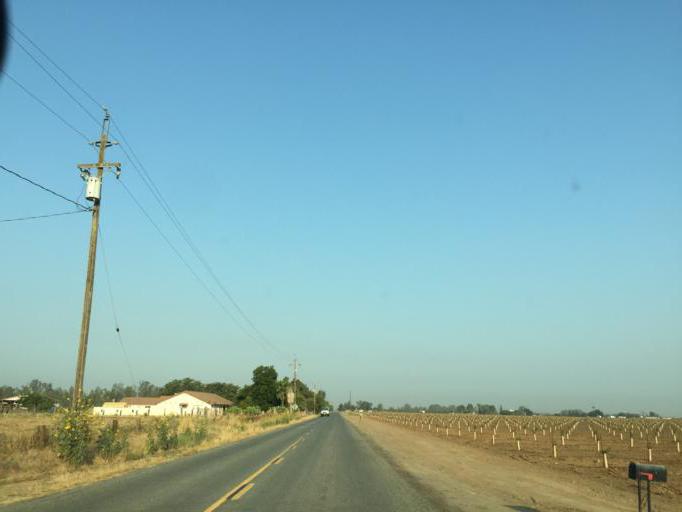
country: US
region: California
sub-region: Tulare County
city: Cutler
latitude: 36.4436
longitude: -119.3235
